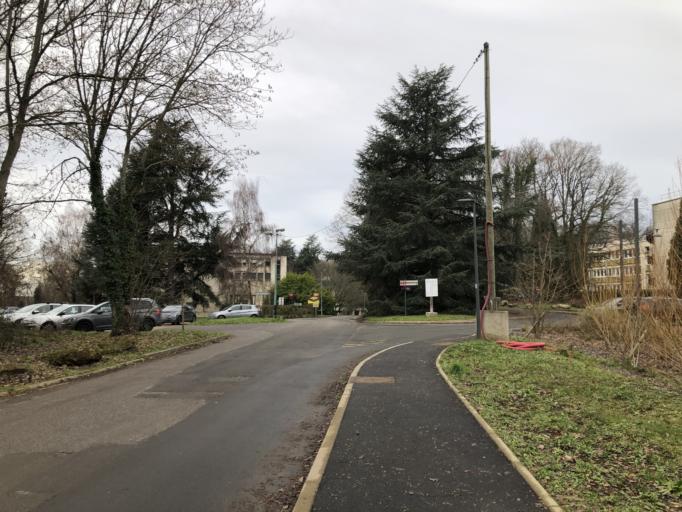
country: FR
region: Ile-de-France
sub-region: Departement de l'Essonne
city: Bures-sur-Yvette
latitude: 48.7066
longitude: 2.1762
